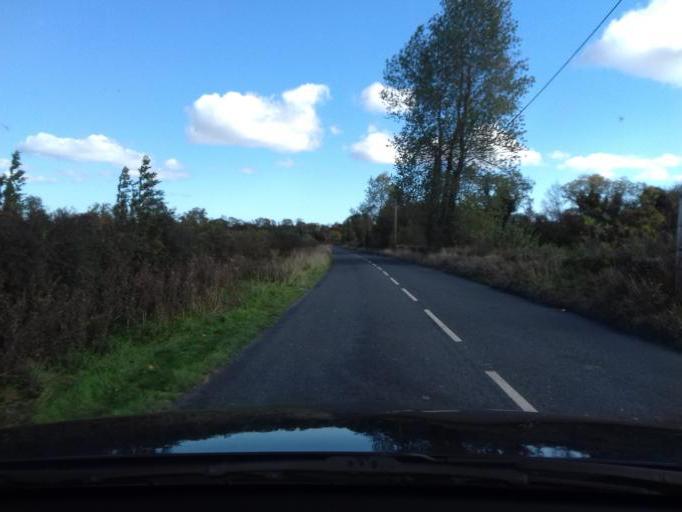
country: IE
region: Leinster
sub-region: An Mhi
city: Slane
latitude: 53.6876
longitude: -6.5097
